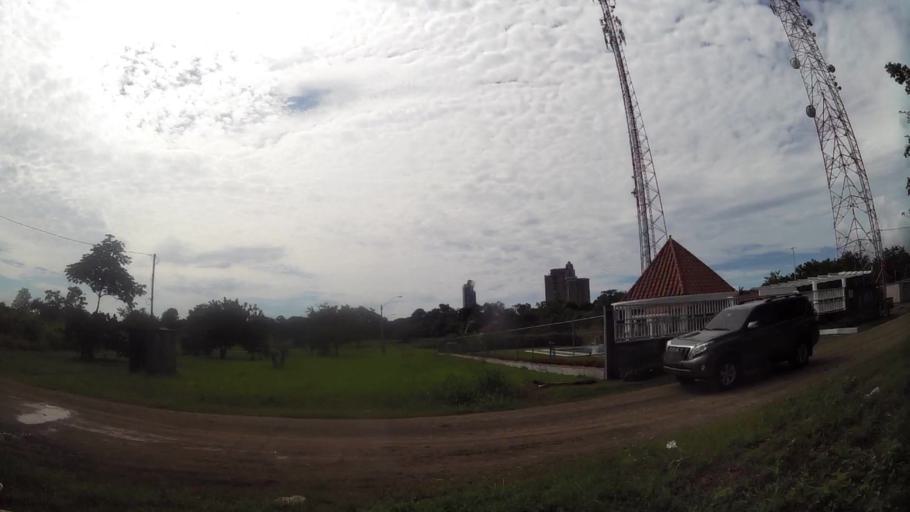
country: PA
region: Panama
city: Nueva Gorgona
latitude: 8.5468
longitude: -79.8851
